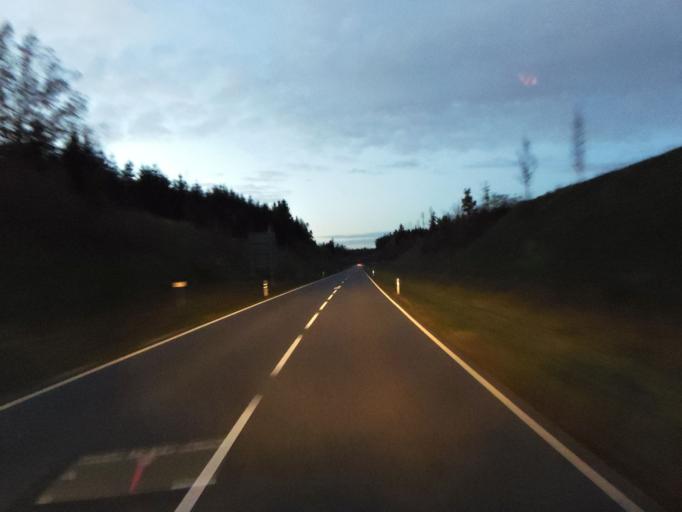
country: DE
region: Bavaria
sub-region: Upper Bavaria
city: Brunnthal
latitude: 48.0145
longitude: 11.6978
